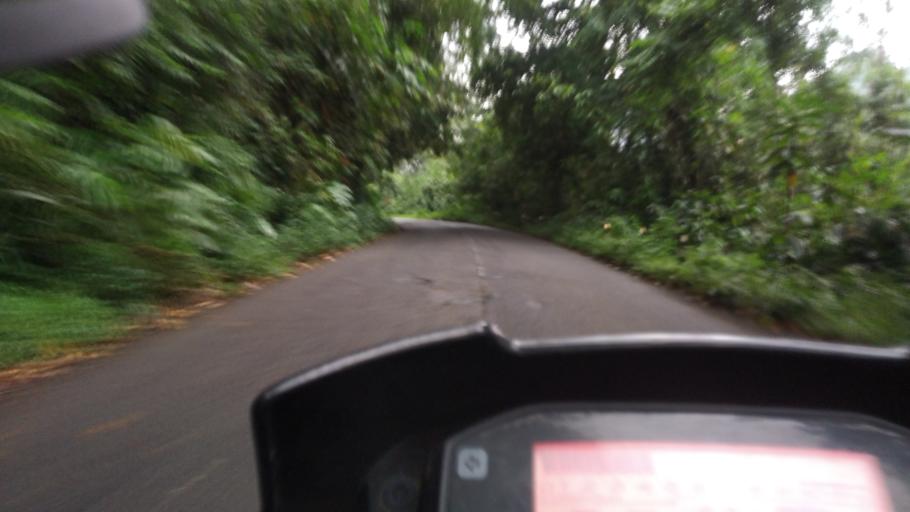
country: IN
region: Kerala
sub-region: Idukki
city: Kuttampuzha
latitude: 10.0636
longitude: 76.7922
